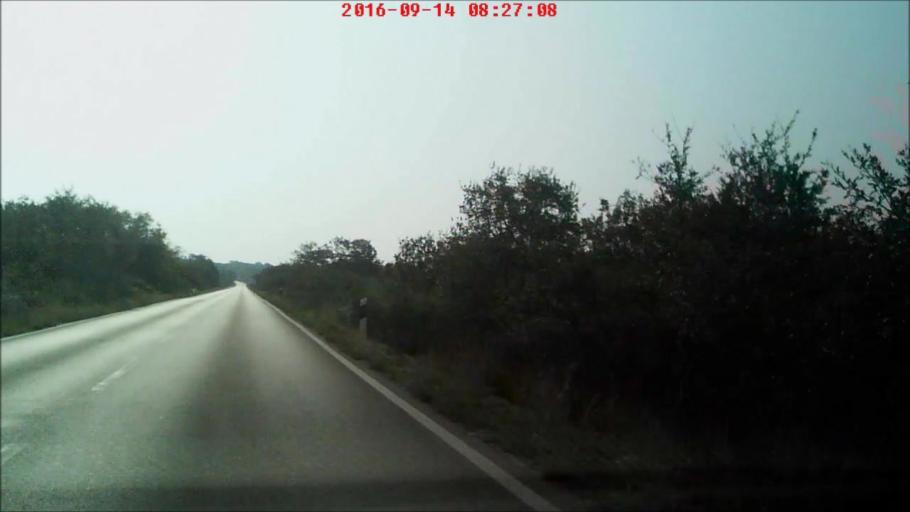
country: HR
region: Zadarska
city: Zadar
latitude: 44.1908
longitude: 15.2626
